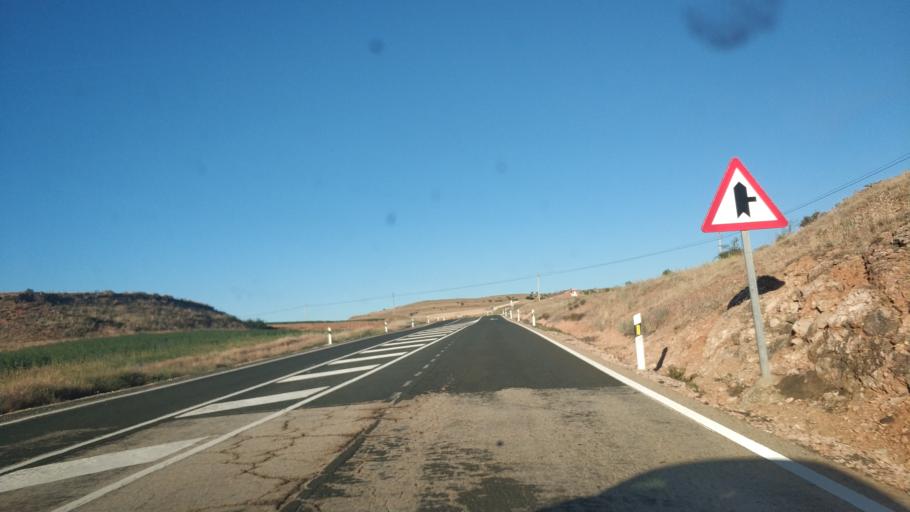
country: ES
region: Castille and Leon
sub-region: Provincia de Soria
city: El Burgo de Osma
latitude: 41.5762
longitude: -3.0992
